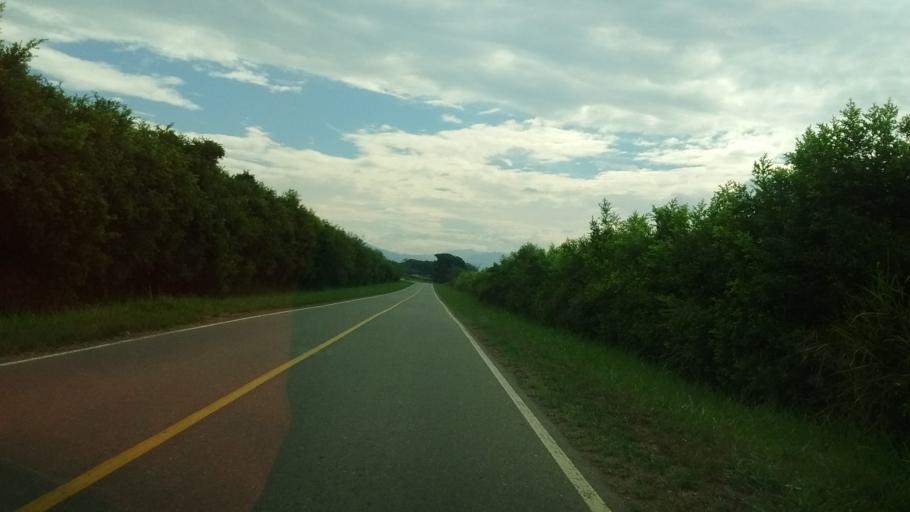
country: CO
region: Cauca
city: Santander de Quilichao
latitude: 3.0406
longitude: -76.4606
